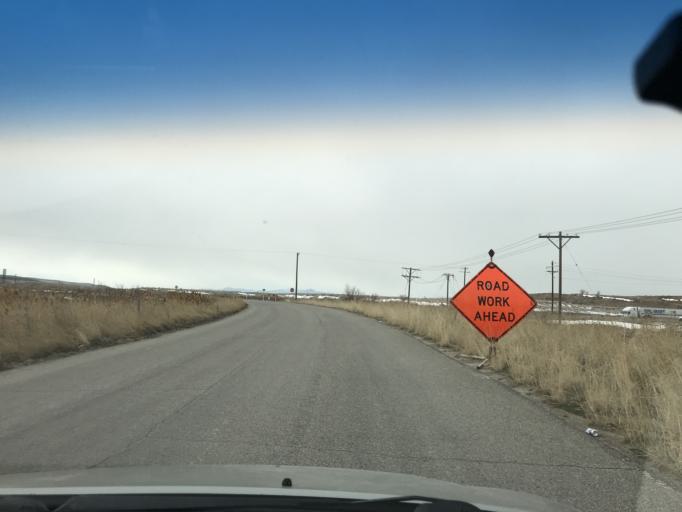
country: US
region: Utah
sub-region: Salt Lake County
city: Magna
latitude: 40.7732
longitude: -112.0617
